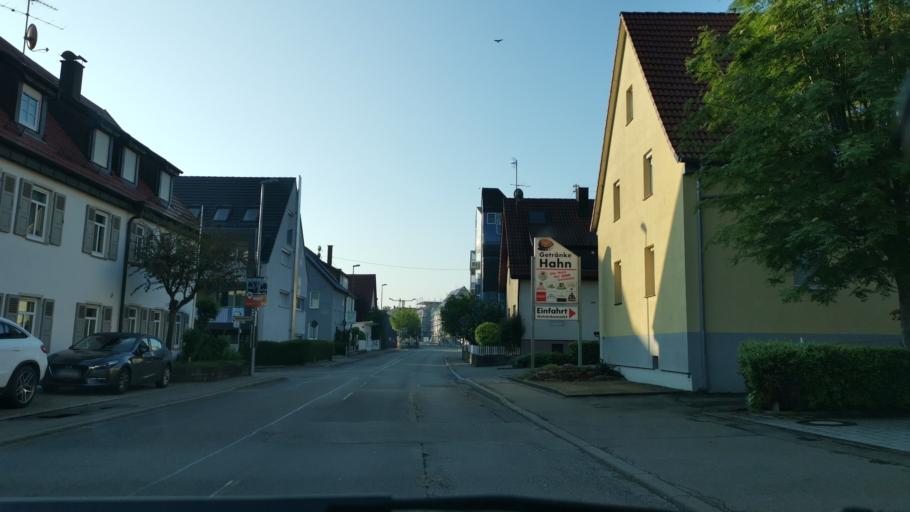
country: DE
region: Baden-Wuerttemberg
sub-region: Regierungsbezirk Stuttgart
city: Ehningen
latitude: 48.6923
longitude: 8.9474
